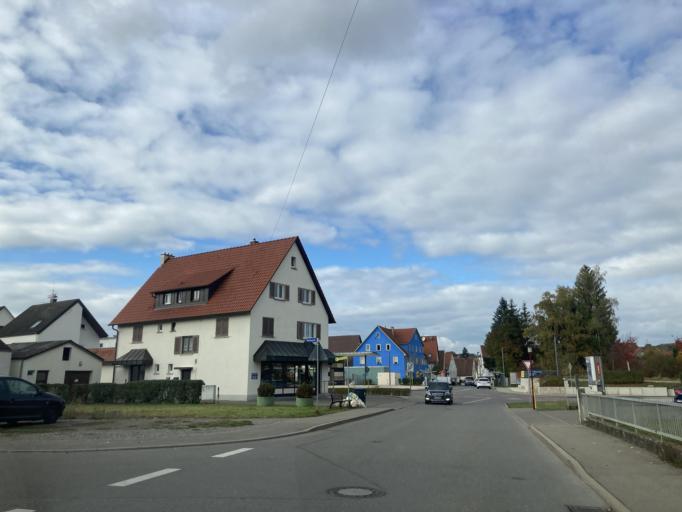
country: DE
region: Baden-Wuerttemberg
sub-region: Tuebingen Region
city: Dusslingen
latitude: 48.4497
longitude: 9.0605
